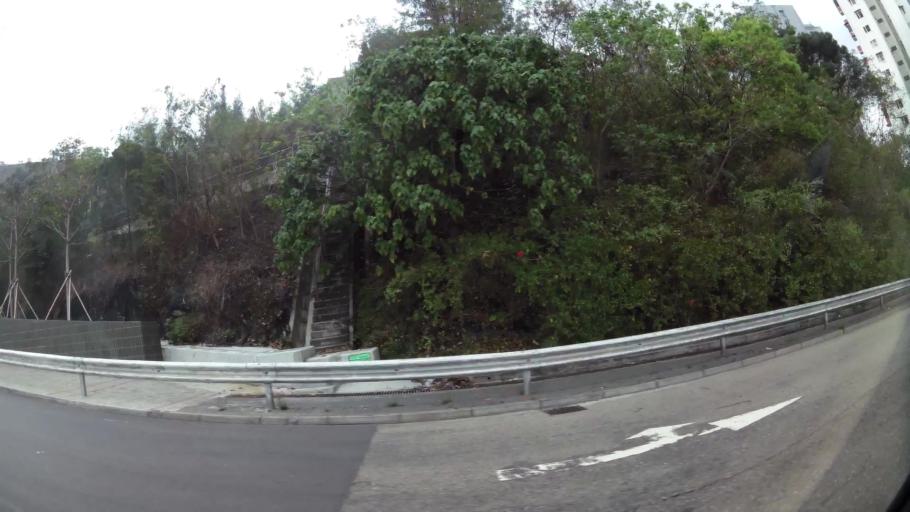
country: HK
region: Kowloon City
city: Kowloon
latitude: 22.3109
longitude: 114.1838
